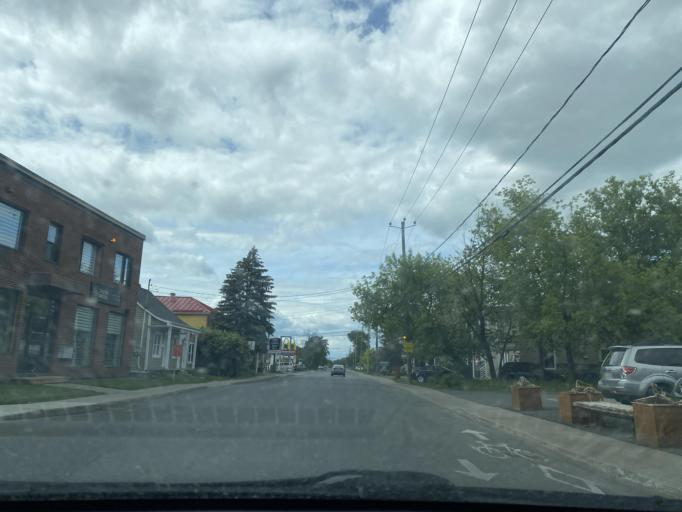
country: CA
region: Quebec
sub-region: Monteregie
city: Carignan
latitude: 45.4522
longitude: -73.2976
